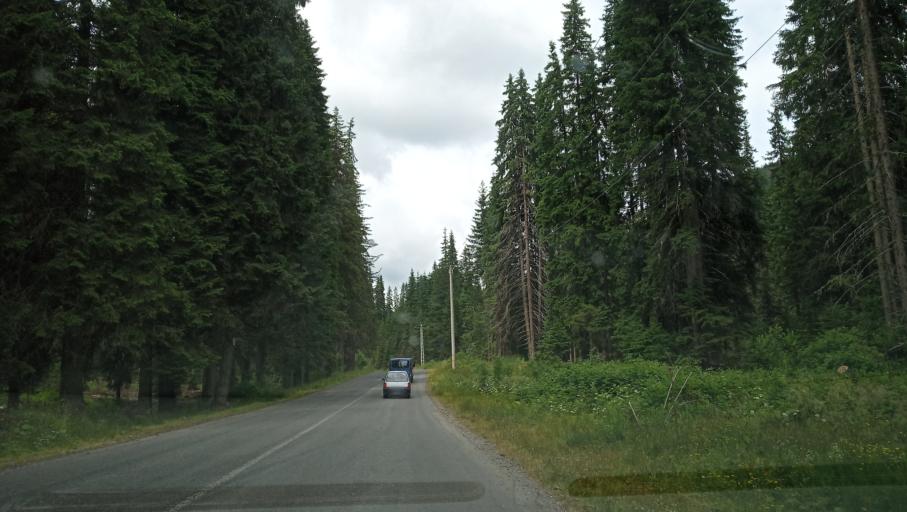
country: RO
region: Gorj
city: Novaci-Straini
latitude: 45.4317
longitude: 23.6654
